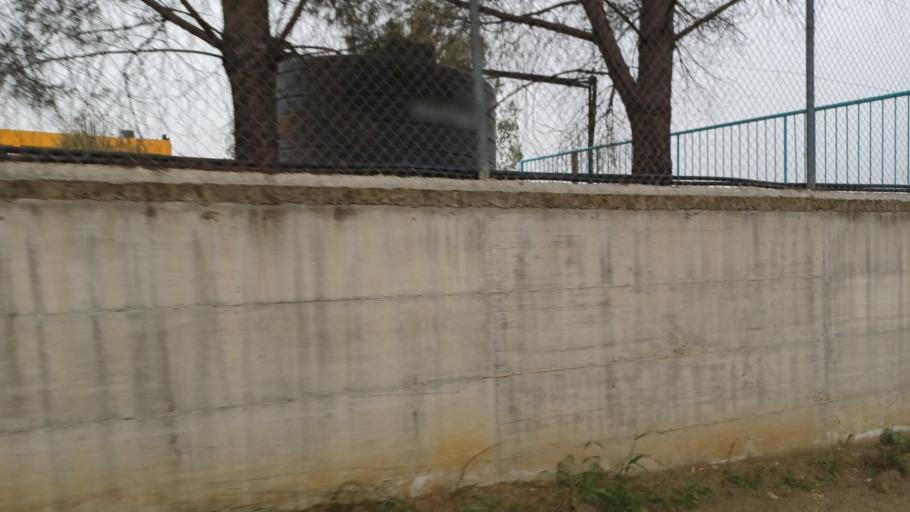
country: CY
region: Limassol
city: Parekklisha
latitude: 34.8475
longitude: 33.1438
